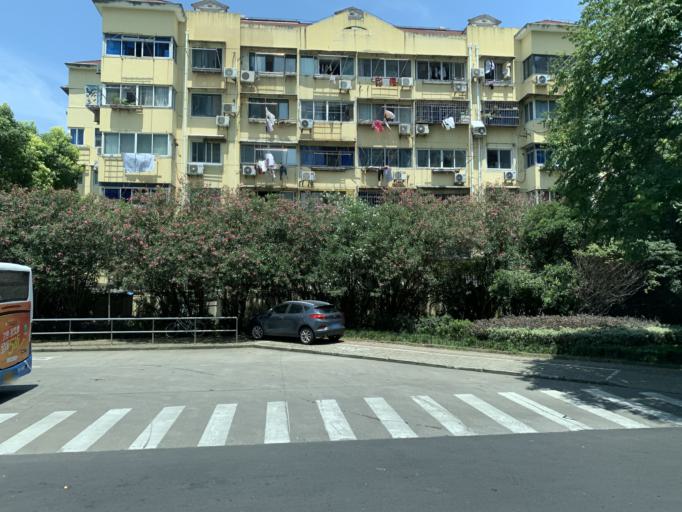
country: CN
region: Shanghai Shi
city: Huamu
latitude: 31.2473
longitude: 121.5786
